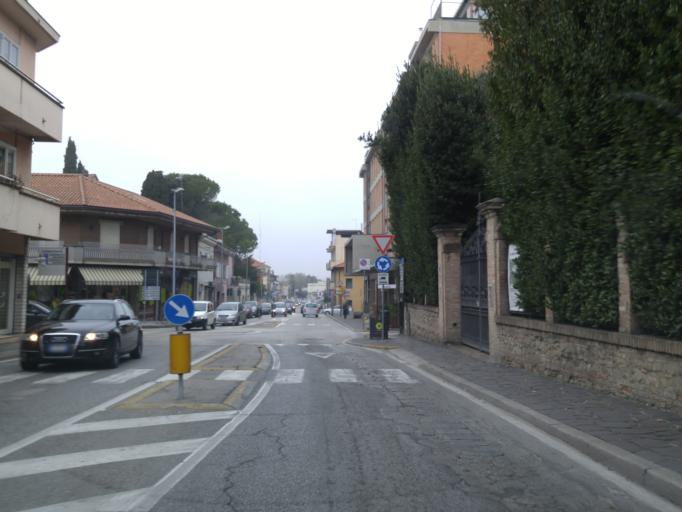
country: IT
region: Emilia-Romagna
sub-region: Provincia di Rimini
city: Cattolica
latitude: 43.9628
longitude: 12.7416
